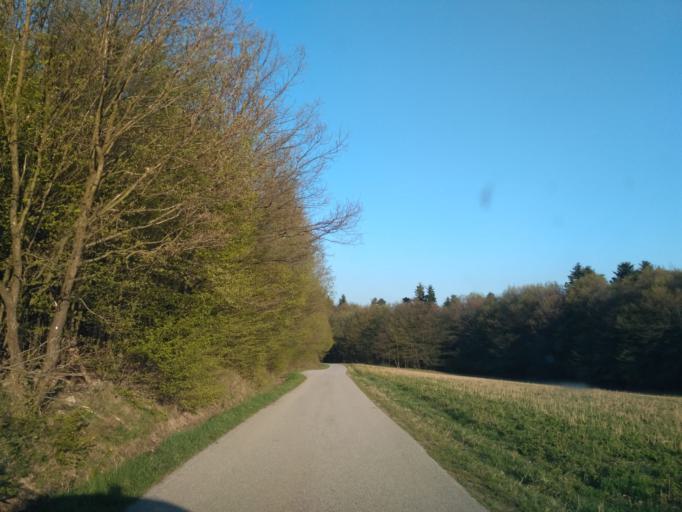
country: SK
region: Kosicky
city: Kosice
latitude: 48.7317
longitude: 21.1741
